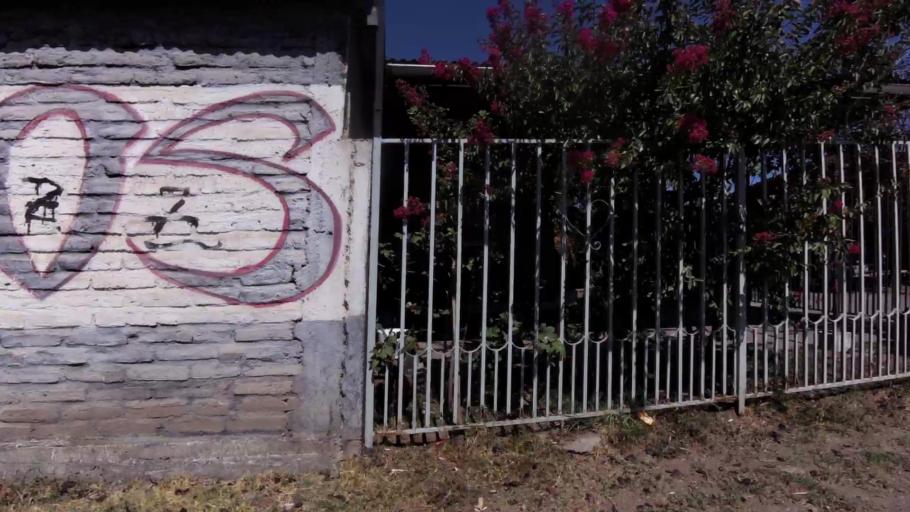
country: CL
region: O'Higgins
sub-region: Provincia de Cachapoal
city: Rancagua
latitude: -34.1700
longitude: -70.7664
